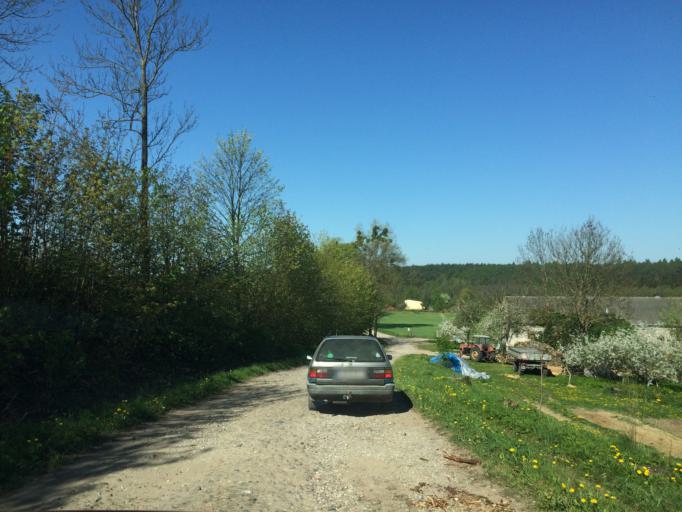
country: PL
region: Warmian-Masurian Voivodeship
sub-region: Powiat nowomiejski
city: Biskupiec
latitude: 53.4875
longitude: 19.4773
